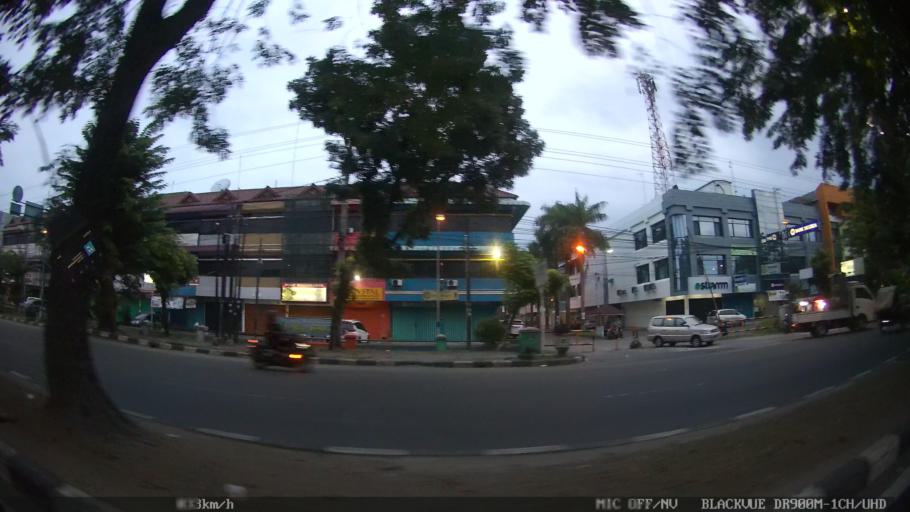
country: ID
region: North Sumatra
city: Medan
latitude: 3.5909
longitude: 98.6410
